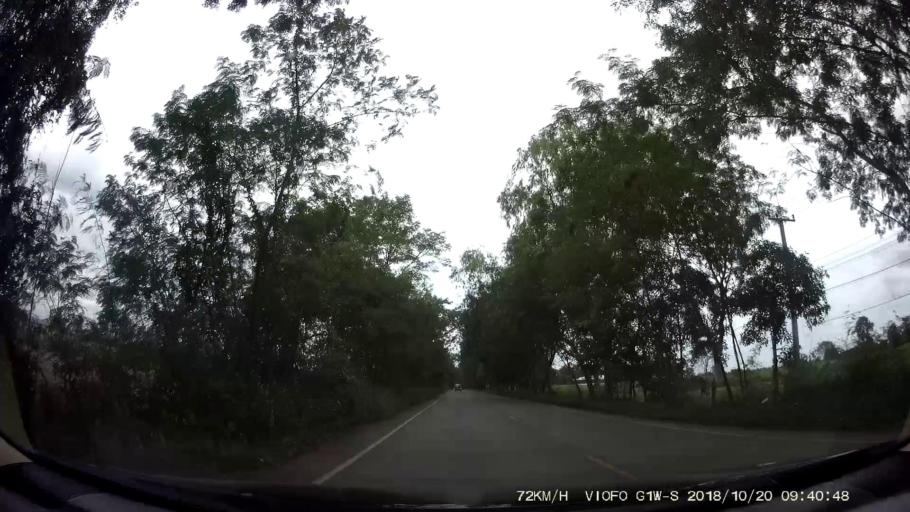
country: TH
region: Chaiyaphum
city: Kaset Sombun
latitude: 16.4466
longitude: 101.9599
